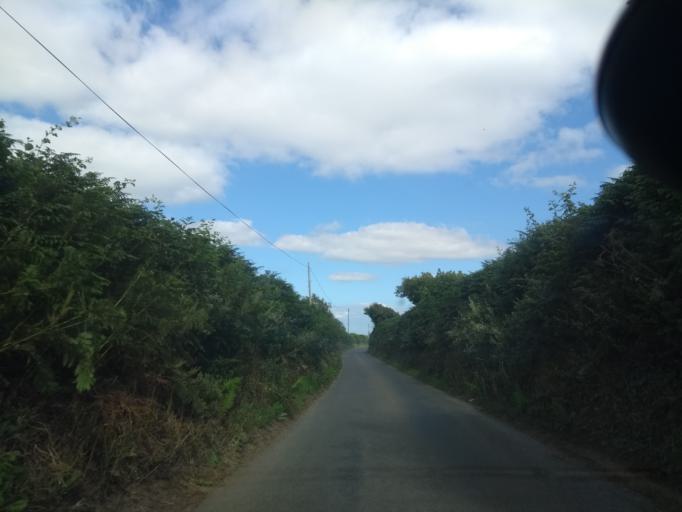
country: GB
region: England
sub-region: Devon
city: Modbury
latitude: 50.3064
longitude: -3.8677
